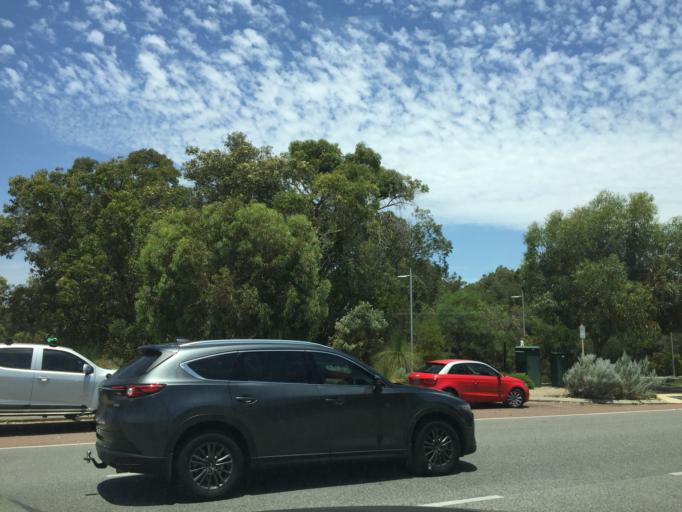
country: AU
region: Western Australia
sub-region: Melville
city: Winthrop
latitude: -32.0712
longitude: 115.8472
